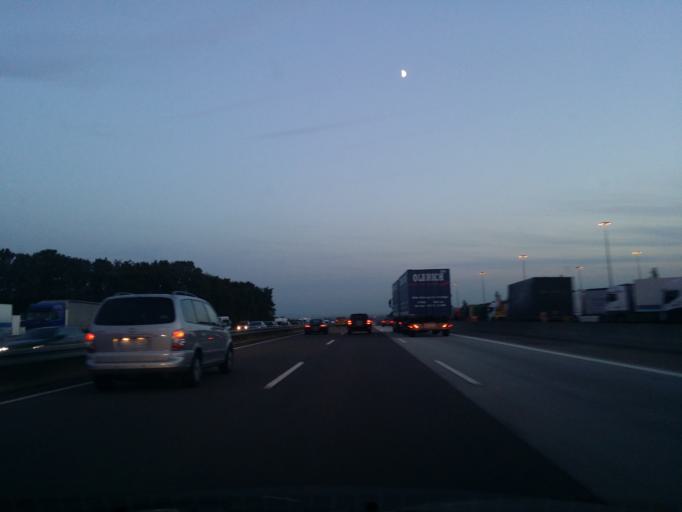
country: DE
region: Hesse
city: Eppstein
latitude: 50.0955
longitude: 8.3530
